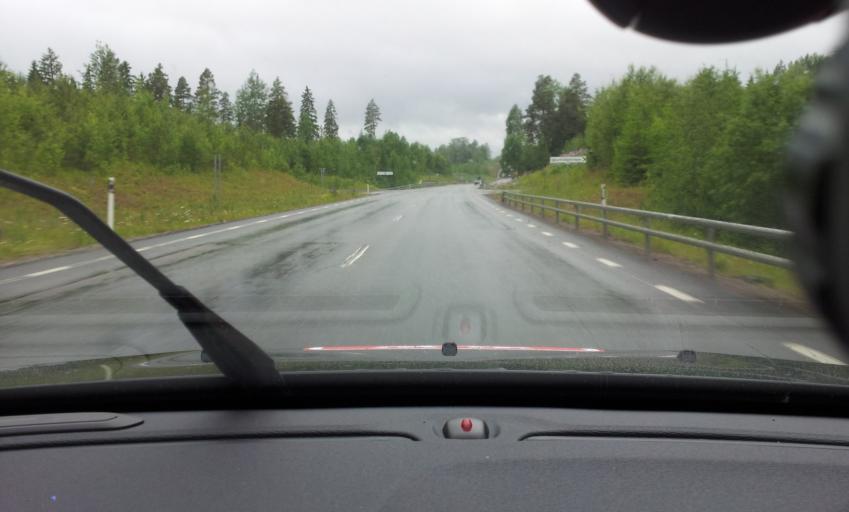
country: SE
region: Jaemtland
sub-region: Ragunda Kommun
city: Hammarstrand
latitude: 63.0322
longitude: 16.5935
